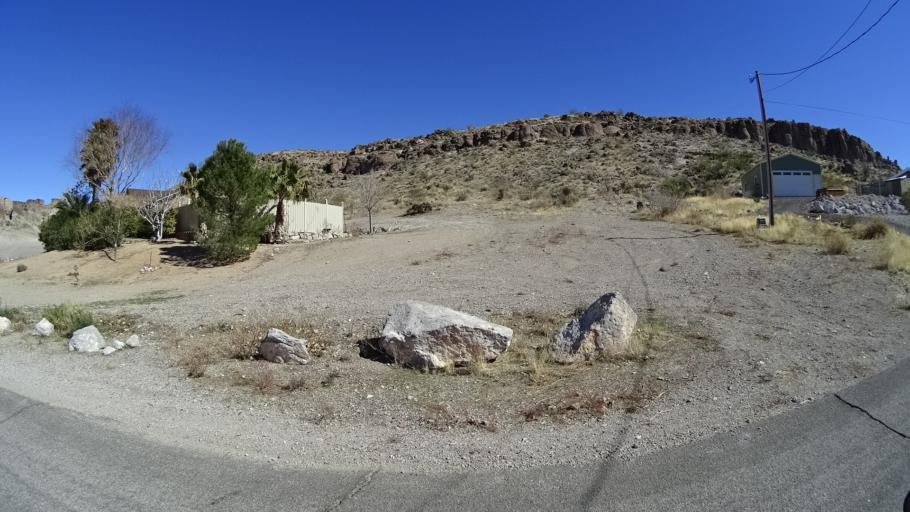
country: US
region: Arizona
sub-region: Mohave County
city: Kingman
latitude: 35.2032
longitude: -114.0622
